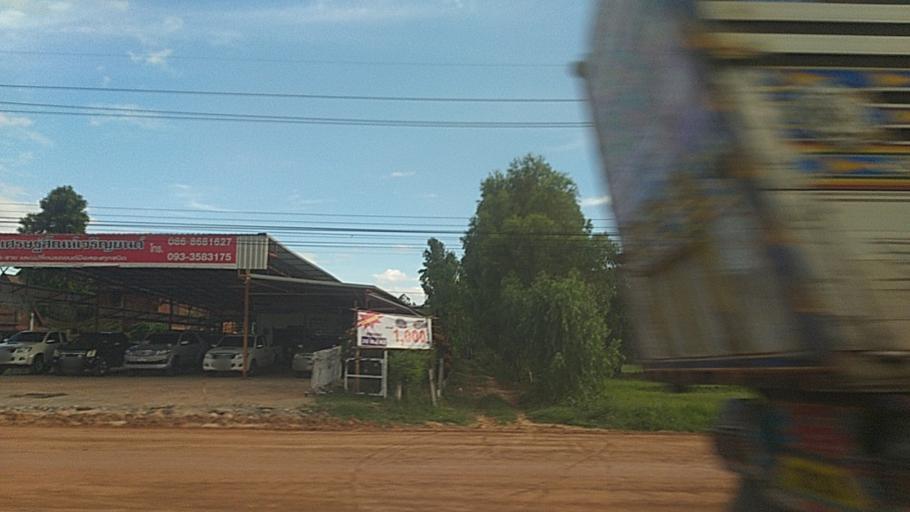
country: TH
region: Surin
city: Kap Choeng
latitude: 14.4592
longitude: 103.6649
